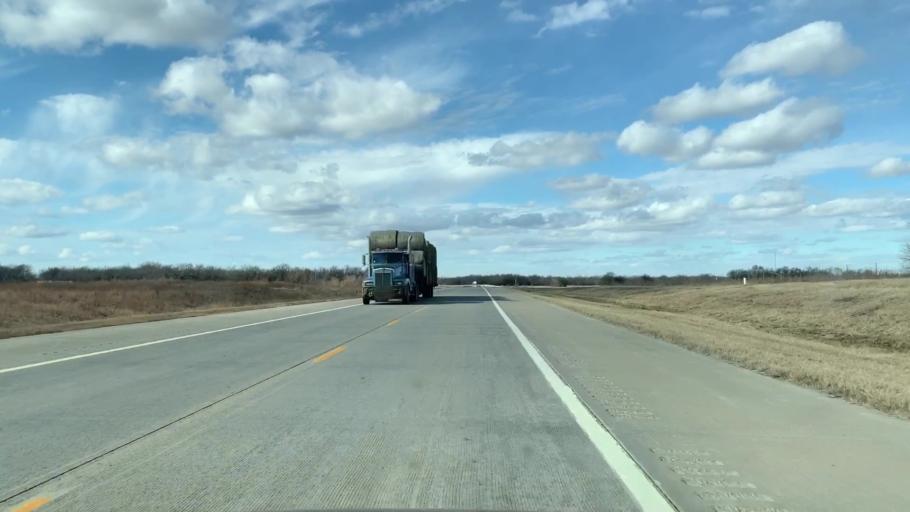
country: US
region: Kansas
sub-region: Labette County
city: Parsons
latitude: 37.3544
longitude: -95.2126
